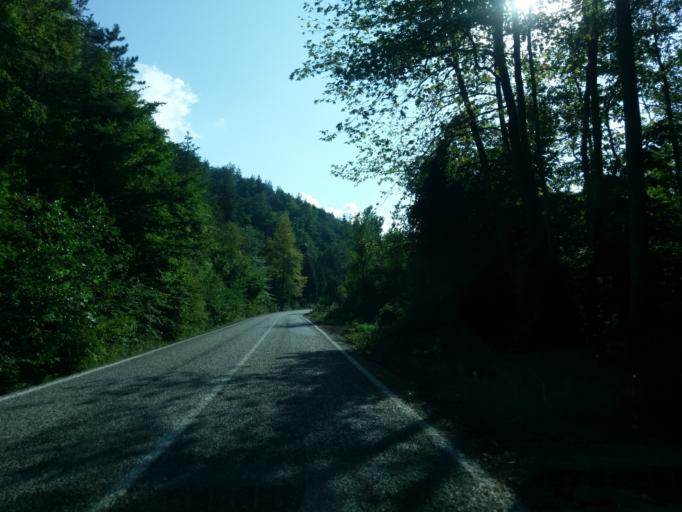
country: TR
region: Sinop
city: Yenikonak
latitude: 41.8833
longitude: 34.5634
